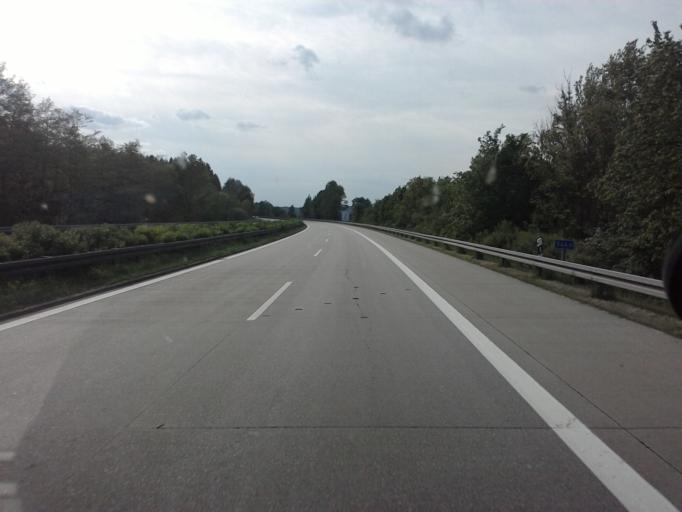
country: DE
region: Bavaria
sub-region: Lower Bavaria
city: Windberg
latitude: 48.9106
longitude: 12.7671
